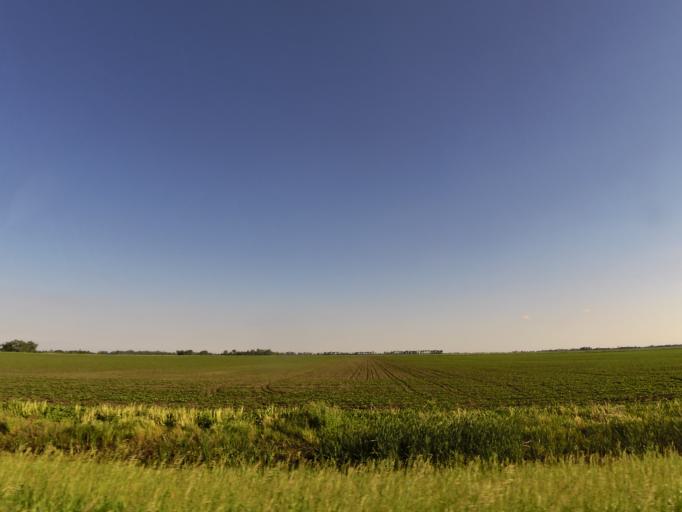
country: US
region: North Dakota
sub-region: Grand Forks County
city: Grand Forks Air Force Base
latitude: 48.1357
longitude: -97.2414
